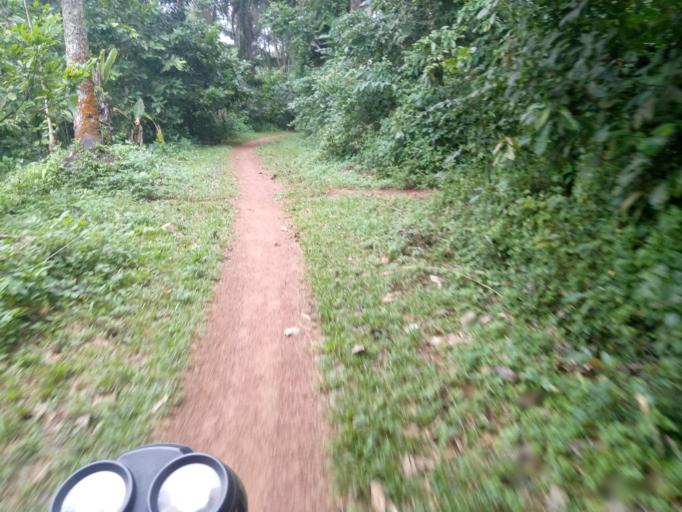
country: SL
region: Eastern Province
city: Buedu
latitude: 8.4798
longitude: -10.3318
